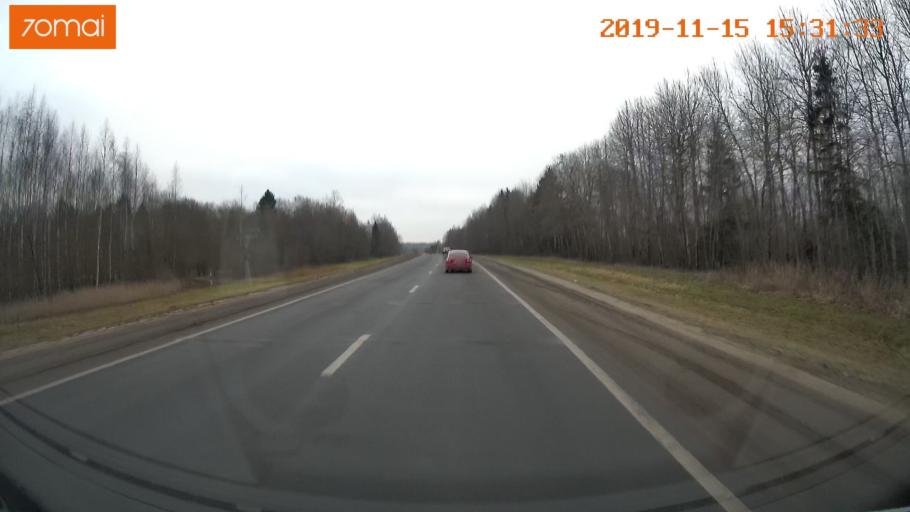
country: RU
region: Jaroslavl
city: Danilov
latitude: 58.0992
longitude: 40.1066
